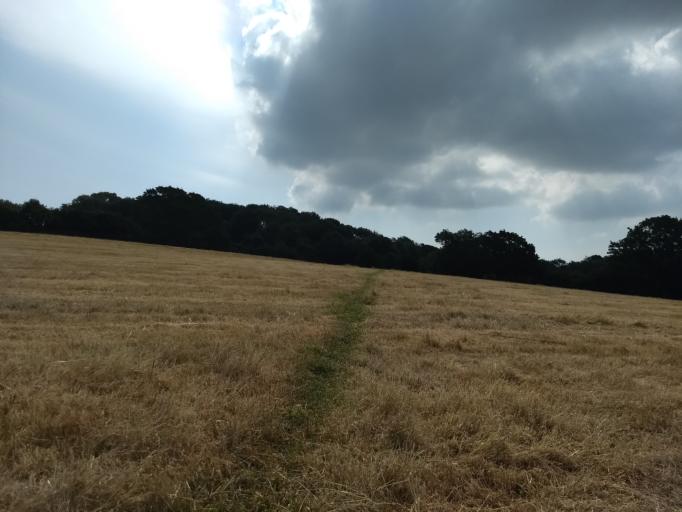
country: GB
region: England
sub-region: Isle of Wight
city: Ryde
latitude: 50.7105
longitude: -1.1528
